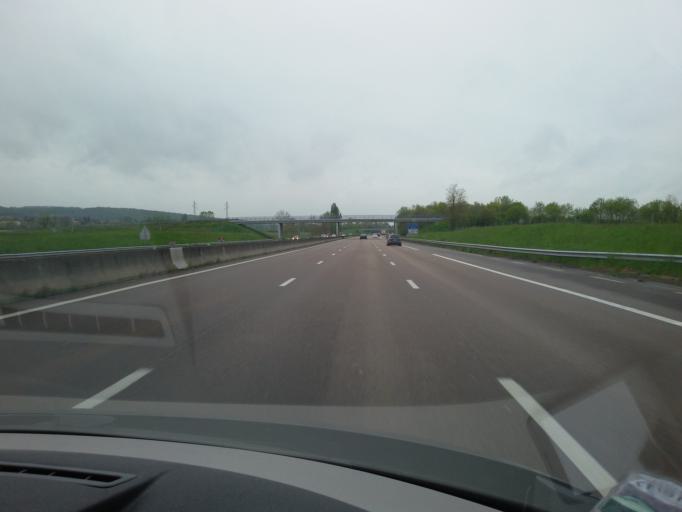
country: FR
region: Bourgogne
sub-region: Departement de Saone-et-Loire
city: Tournus
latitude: 46.4934
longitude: 4.8977
